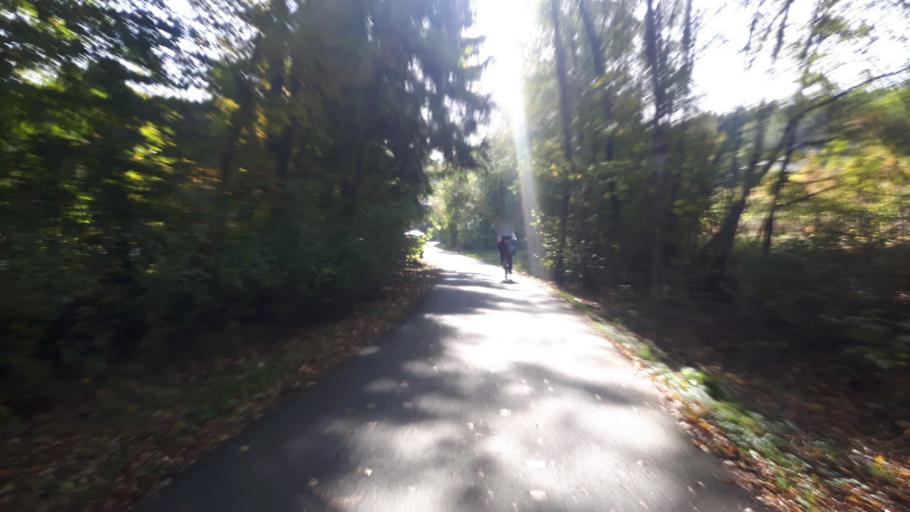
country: DE
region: North Rhine-Westphalia
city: Netphen
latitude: 50.8852
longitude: 8.1286
